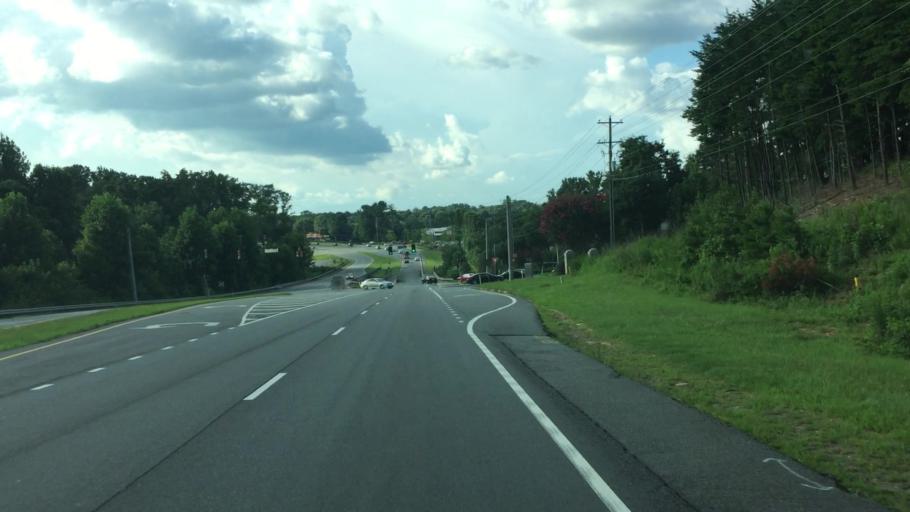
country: US
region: Georgia
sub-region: Fulton County
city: Johns Creek
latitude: 34.1047
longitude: -84.2168
